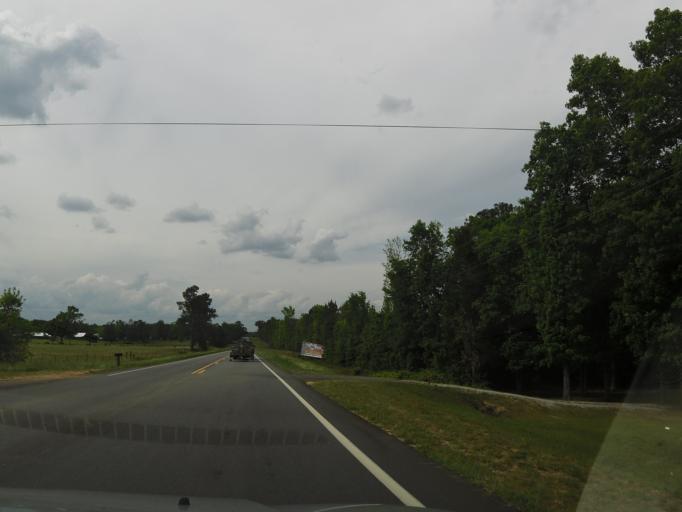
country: US
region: Georgia
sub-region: McDuffie County
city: Thomson
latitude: 33.4185
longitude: -82.4835
